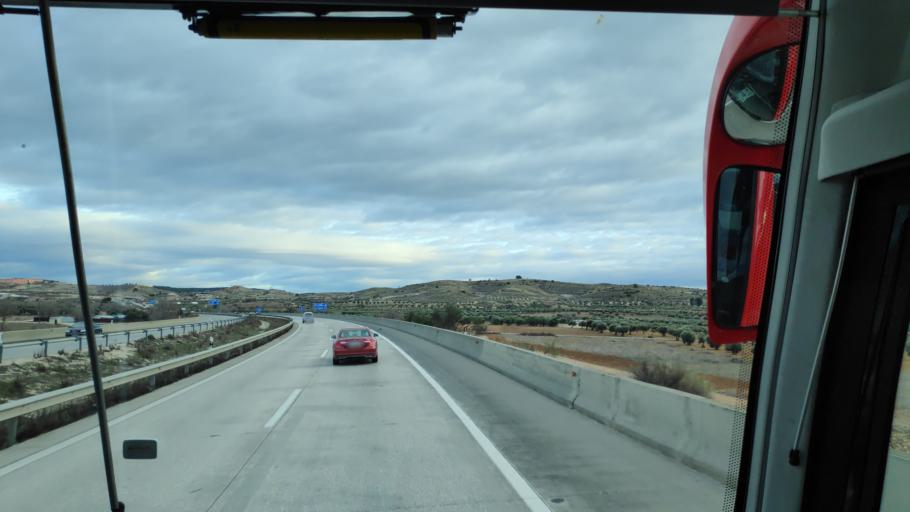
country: ES
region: Madrid
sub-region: Provincia de Madrid
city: Vaciamadrid
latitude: 40.2994
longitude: -3.4824
